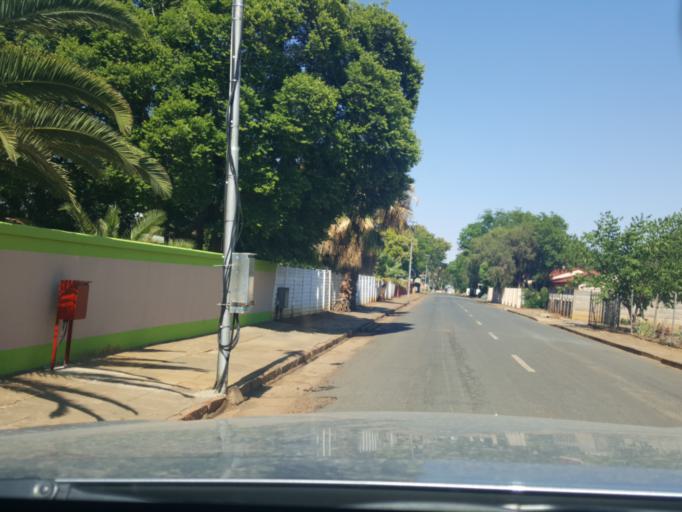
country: ZA
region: North-West
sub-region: Ngaka Modiri Molema District Municipality
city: Zeerust
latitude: -25.5425
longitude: 26.0775
